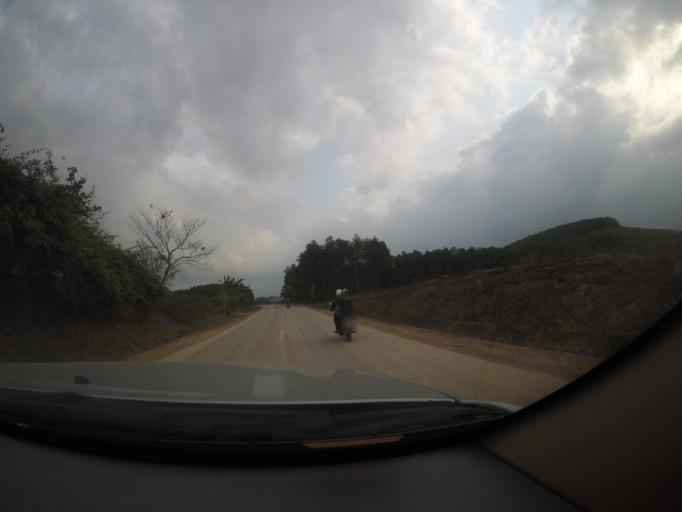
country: VN
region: Quang Tri
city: Ho Xa
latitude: 17.0623
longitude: 106.8613
